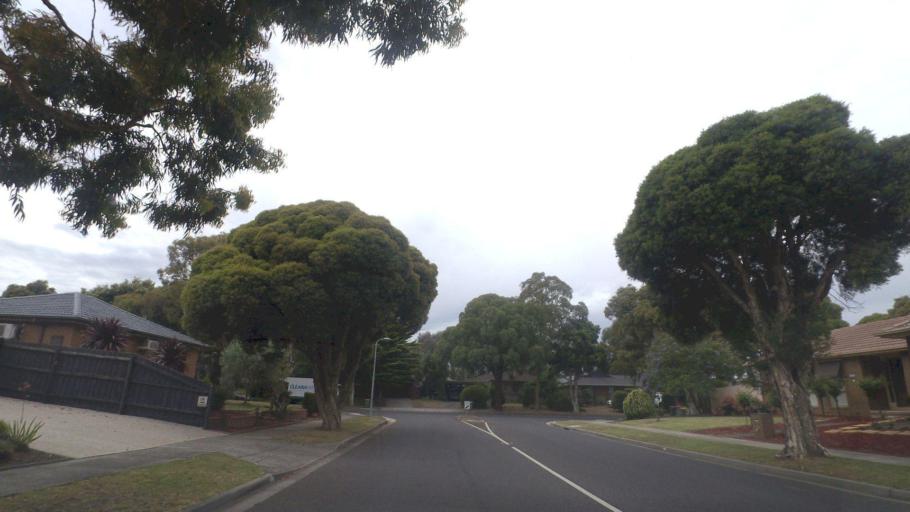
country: AU
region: Victoria
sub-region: Knox
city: Wantirna
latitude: -37.8655
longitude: 145.2355
